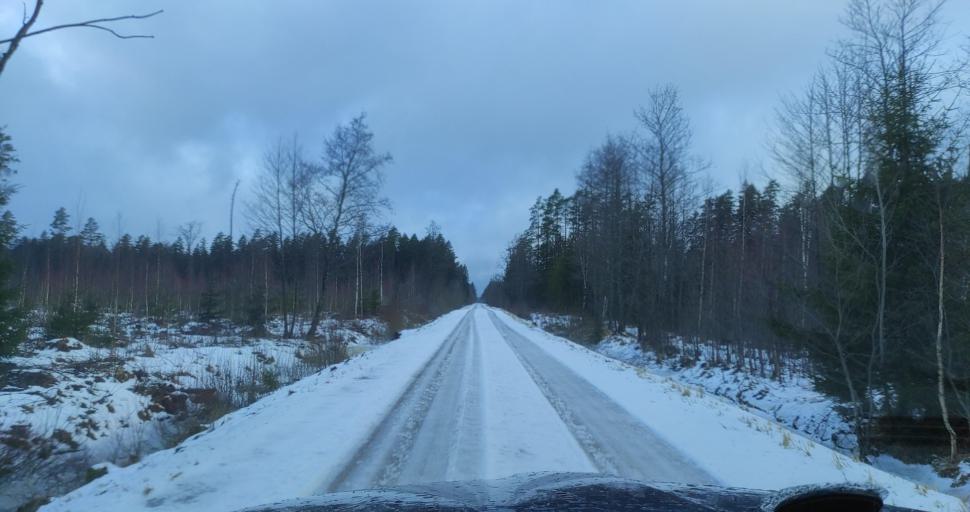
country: LV
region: Dundaga
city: Dundaga
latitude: 57.4061
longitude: 22.0936
